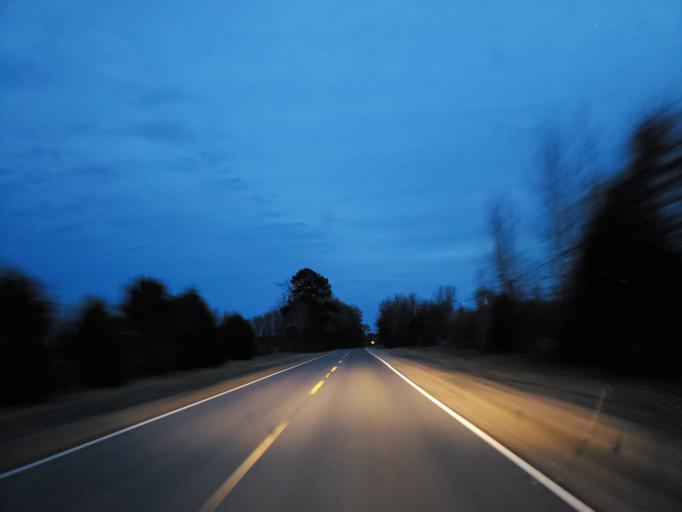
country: US
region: Alabama
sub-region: Greene County
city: Eutaw
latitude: 32.8889
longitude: -87.9459
